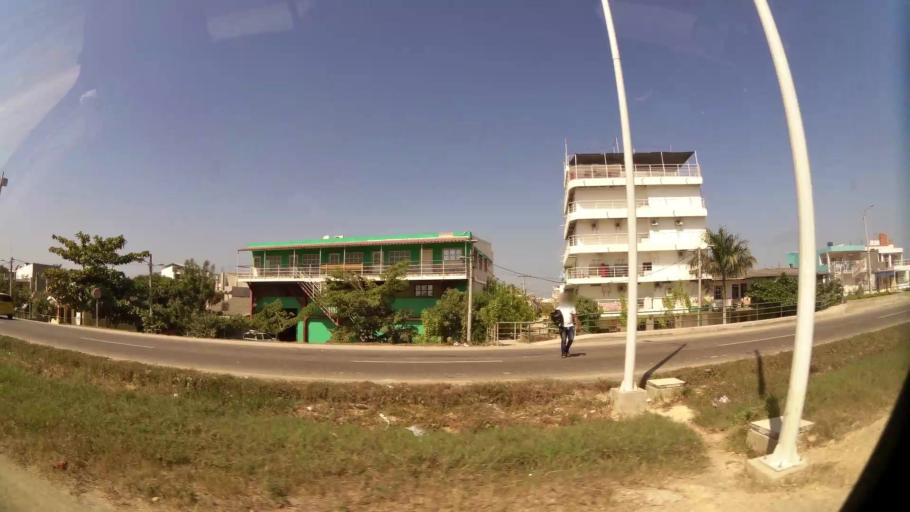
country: CO
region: Bolivar
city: Cartagena
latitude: 10.3833
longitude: -75.4503
